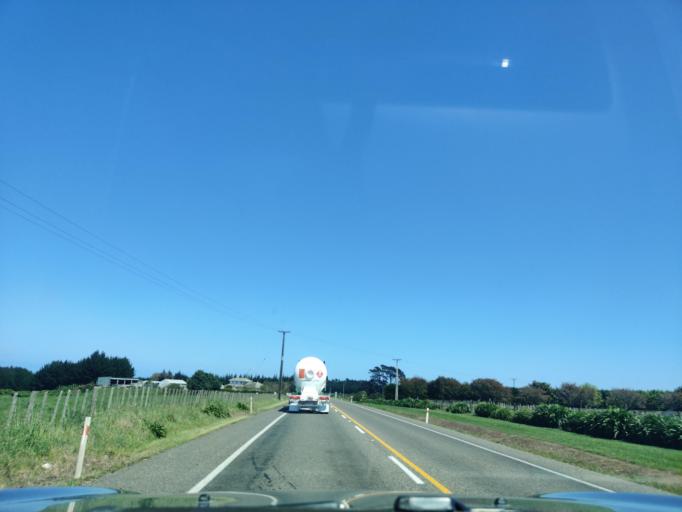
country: NZ
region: Manawatu-Wanganui
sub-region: Wanganui District
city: Wanganui
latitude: -39.8216
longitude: 174.8550
